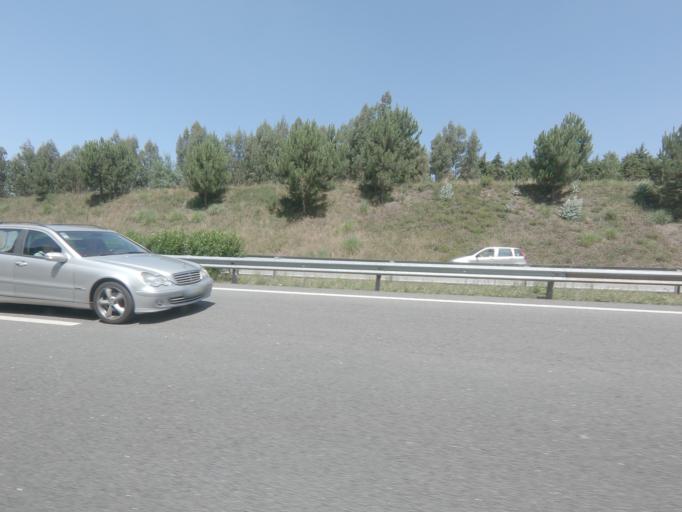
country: PT
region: Porto
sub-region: Gondomar
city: Baguim do Monte
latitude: 41.2023
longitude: -8.5334
